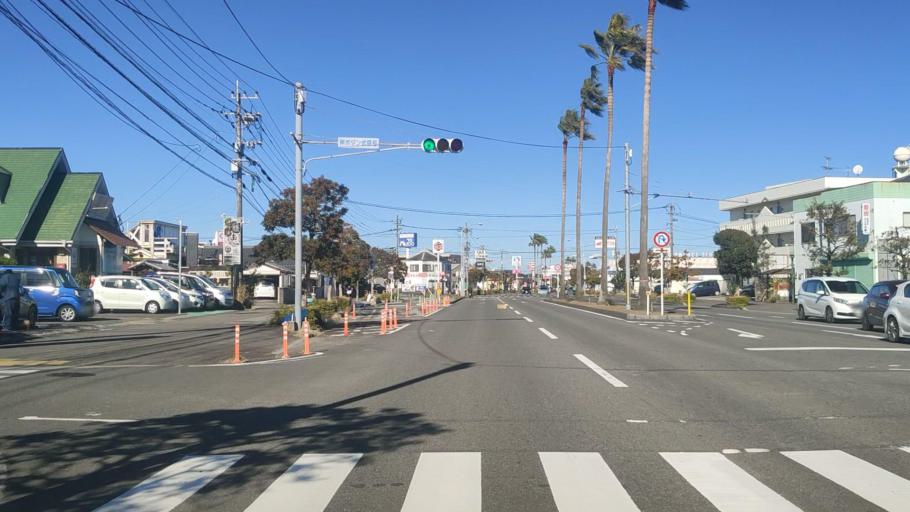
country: JP
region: Miyazaki
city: Miyazaki-shi
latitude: 31.9088
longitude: 131.4470
